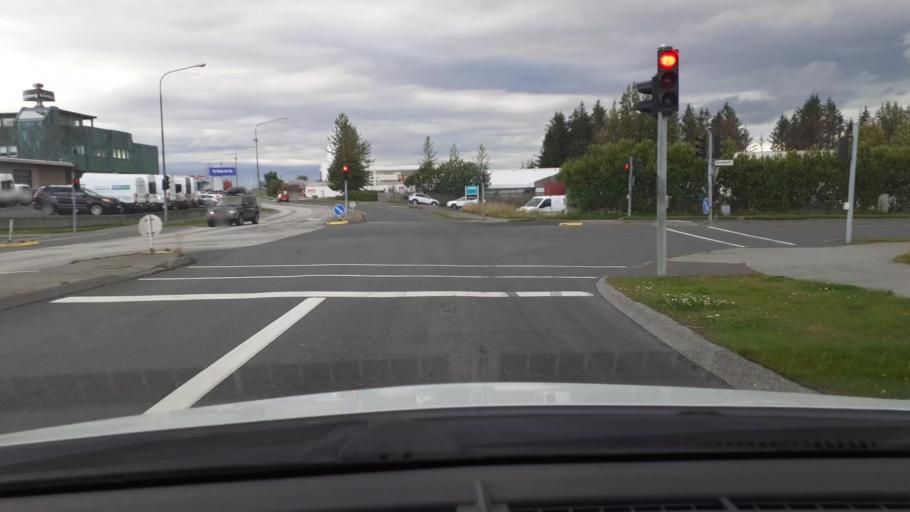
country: IS
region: Capital Region
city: Reykjavik
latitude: 64.1254
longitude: -21.8231
